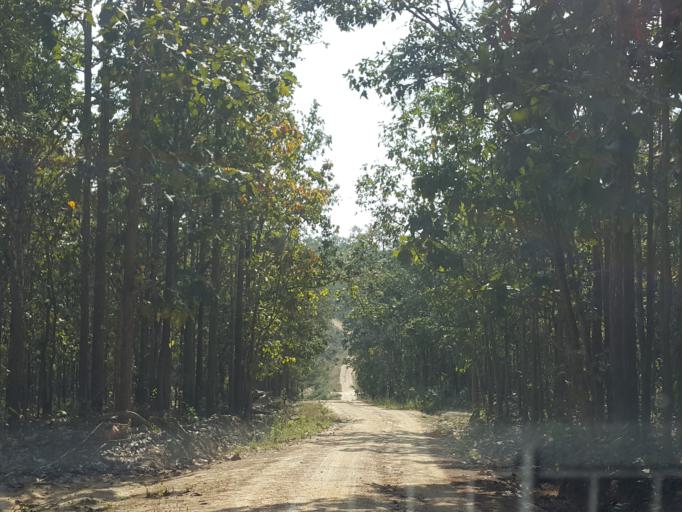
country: TH
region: Chiang Mai
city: Hot
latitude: 18.1518
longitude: 98.4305
